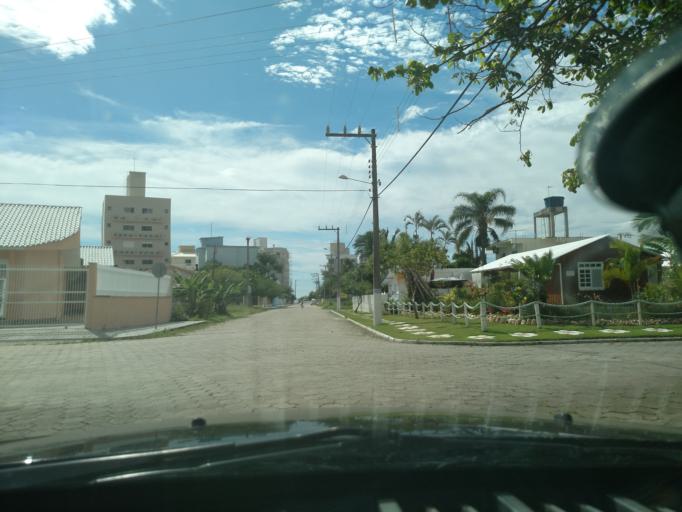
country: BR
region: Santa Catarina
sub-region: Tijucas
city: Tijucas
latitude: -27.3218
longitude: -48.5426
